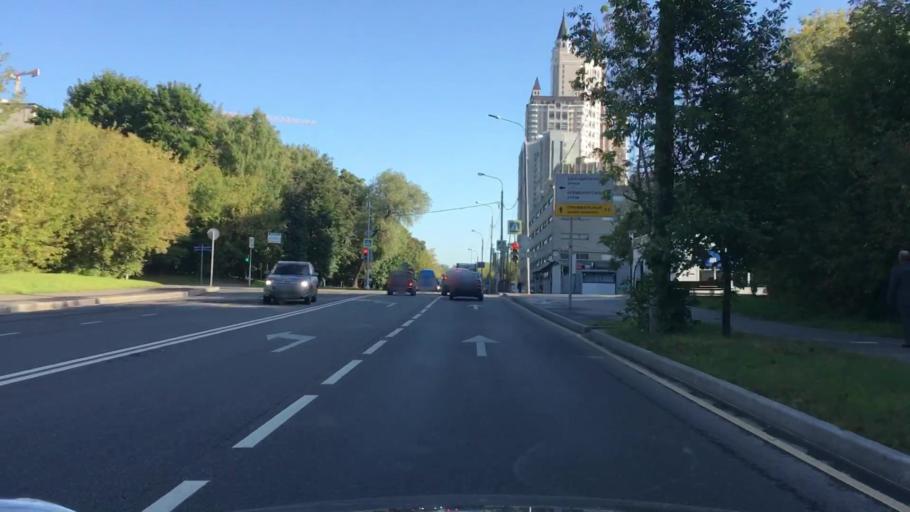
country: RU
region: Moscow
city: Davydkovo
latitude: 55.7223
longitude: 37.4788
